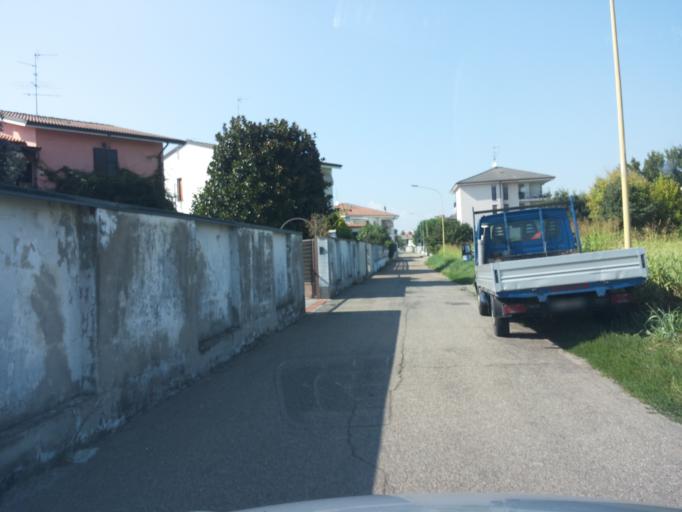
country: IT
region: Piedmont
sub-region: Provincia di Vercelli
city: Vercelli
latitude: 45.3118
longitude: 8.4318
